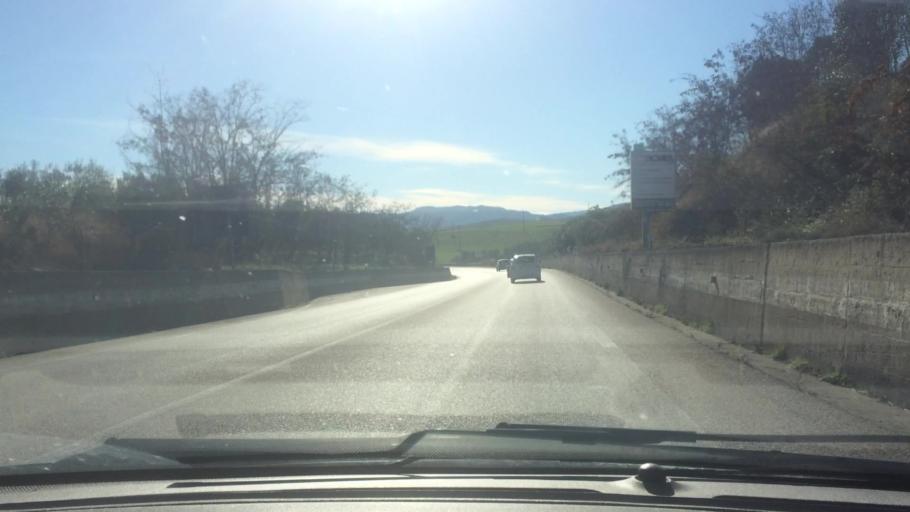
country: IT
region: Basilicate
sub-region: Provincia di Matera
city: Miglionico
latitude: 40.5933
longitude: 16.5734
